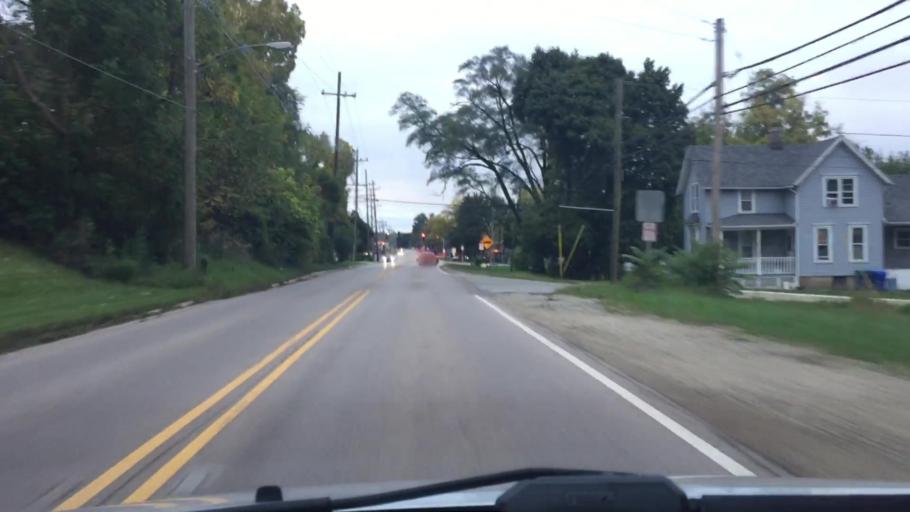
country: US
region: Illinois
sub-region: Kane County
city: South Elgin
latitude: 41.9922
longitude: -88.2971
